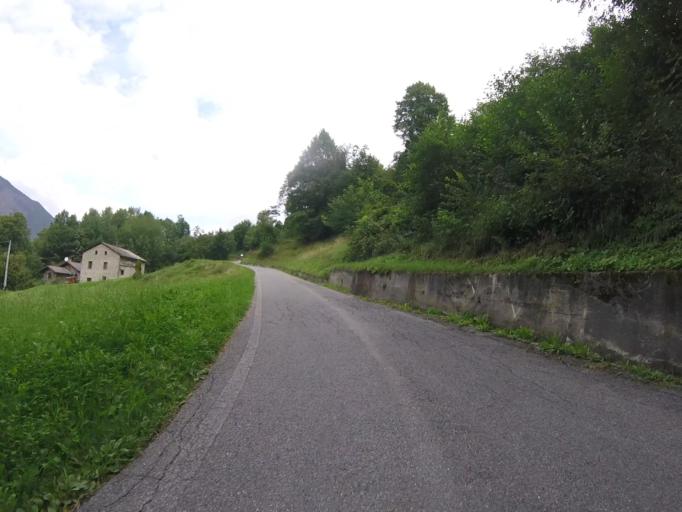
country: IT
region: Lombardy
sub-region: Provincia di Sondrio
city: Mazzo di Valtellina
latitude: 46.2593
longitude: 10.2679
